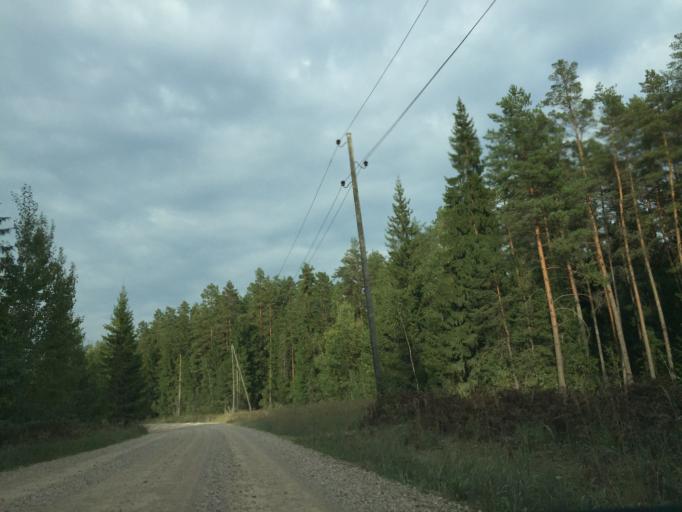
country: LV
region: Ikskile
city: Ikskile
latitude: 56.8015
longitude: 24.4390
